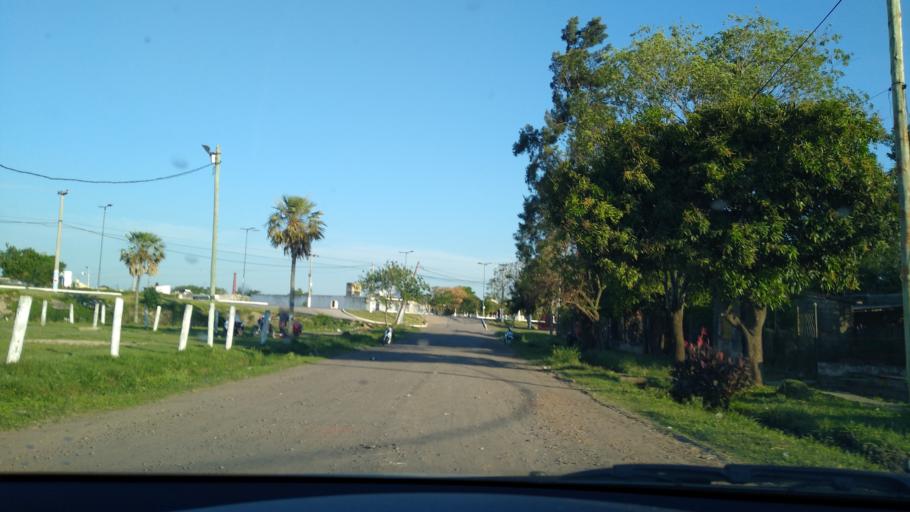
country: AR
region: Chaco
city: Puerto Vilelas
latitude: -27.5155
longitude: -58.9427
